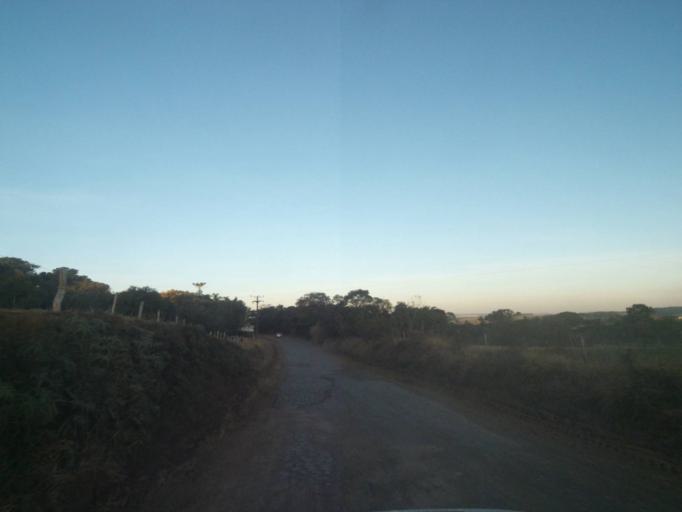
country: BR
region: Parana
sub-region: Tibagi
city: Tibagi
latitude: -24.5268
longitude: -50.4517
